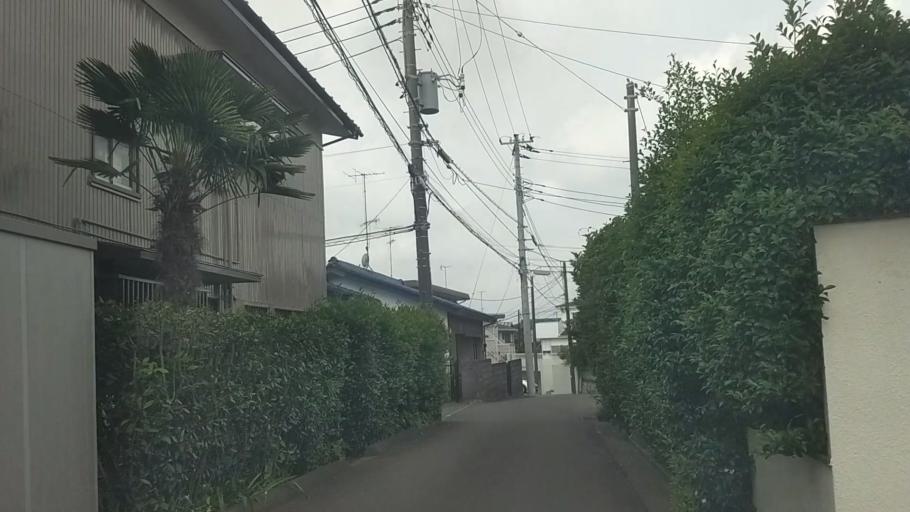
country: JP
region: Kanagawa
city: Fujisawa
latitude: 35.3842
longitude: 139.5085
